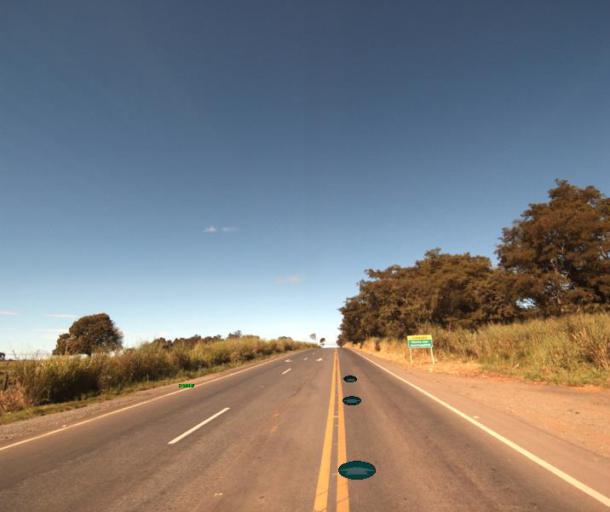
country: BR
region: Goias
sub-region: Itapaci
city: Itapaci
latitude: -14.9884
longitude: -49.4031
